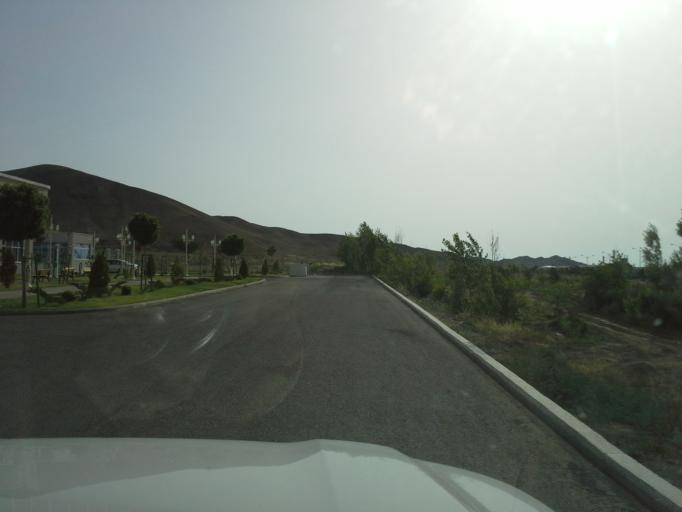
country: TM
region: Balkan
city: Turkmenbasy
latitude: 40.0181
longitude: 52.9691
